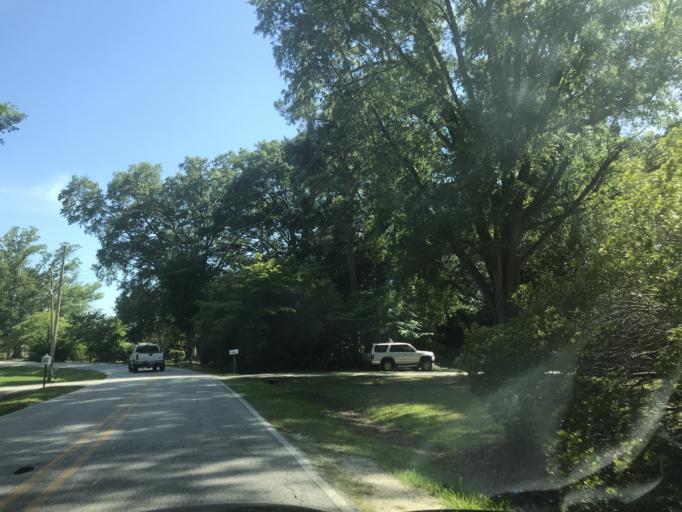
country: US
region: North Carolina
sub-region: Wake County
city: Garner
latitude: 35.7156
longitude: -78.6347
